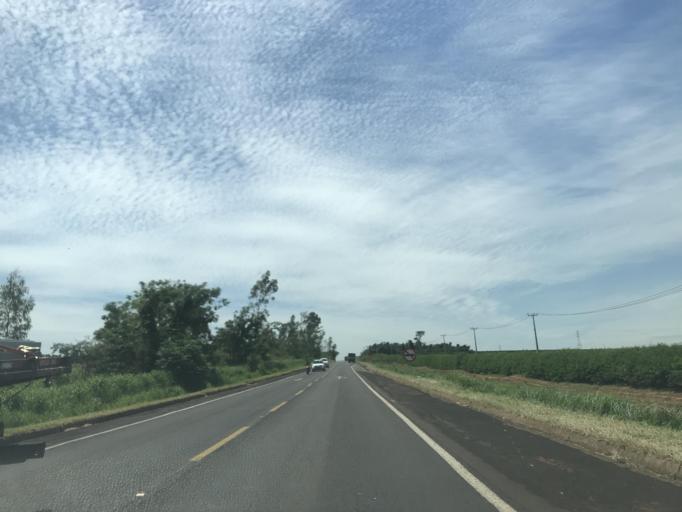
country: BR
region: Parana
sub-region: Paranavai
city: Nova Aurora
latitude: -22.9602
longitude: -52.6494
